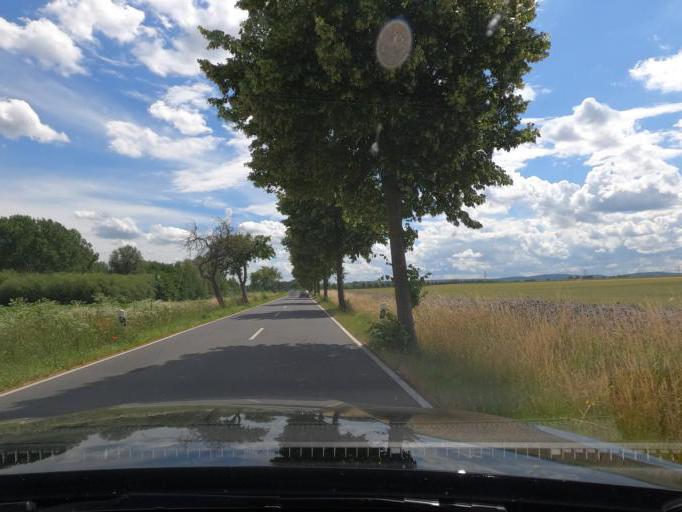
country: DE
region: Lower Saxony
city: Lengede
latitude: 52.1891
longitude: 10.3157
